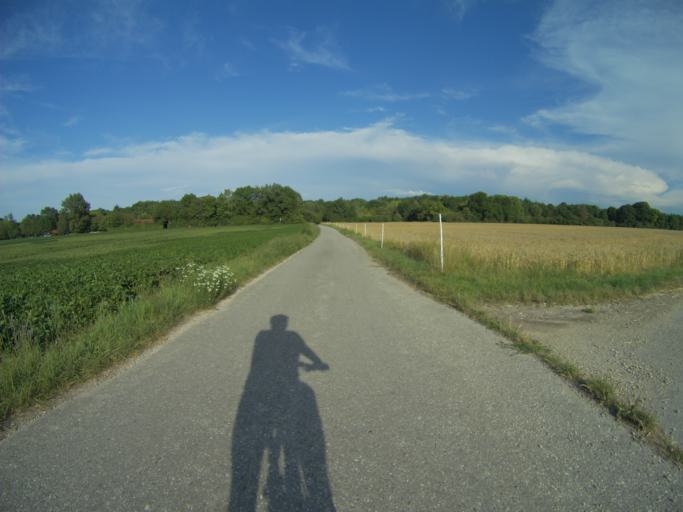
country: DE
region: Bavaria
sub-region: Upper Bavaria
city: Neufahrn bei Freising
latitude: 48.3118
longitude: 11.6918
